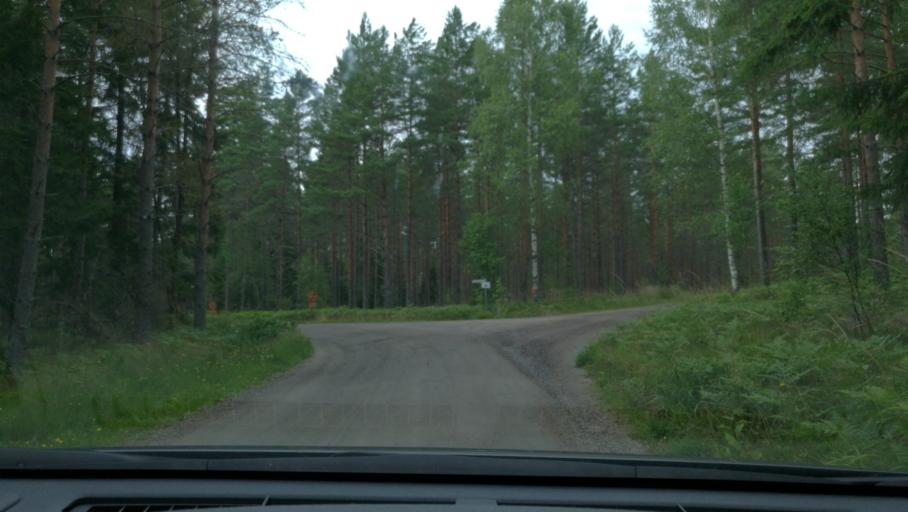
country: SE
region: OEstergoetland
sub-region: Norrkopings Kommun
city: Svartinge
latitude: 58.7578
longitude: 15.9762
